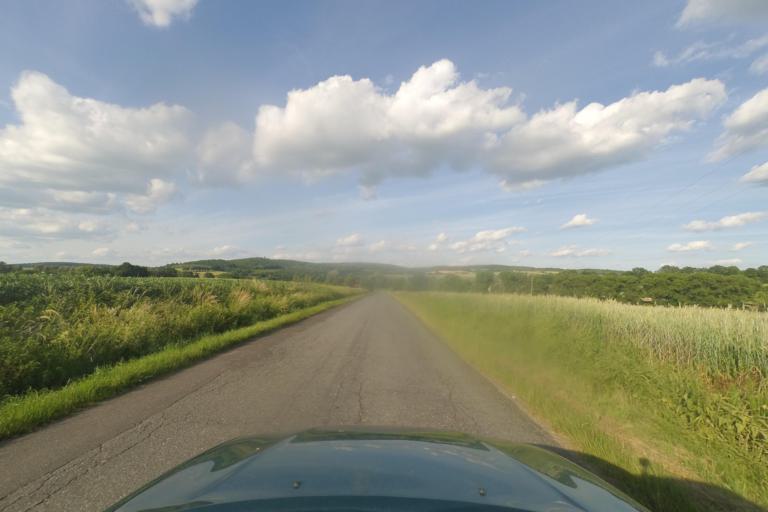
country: PL
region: Lower Silesian Voivodeship
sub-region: Powiat dzierzoniowski
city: Niemcza
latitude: 50.6901
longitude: 16.8444
